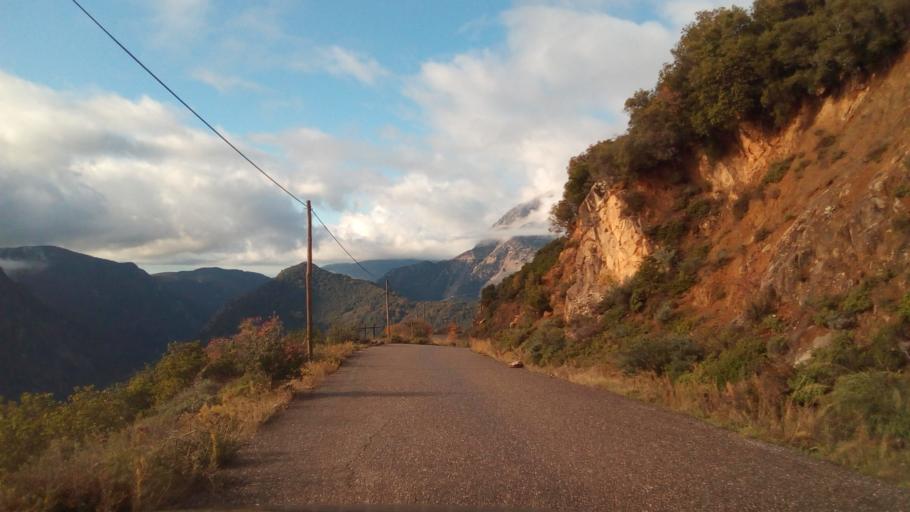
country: GR
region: West Greece
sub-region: Nomos Aitolias kai Akarnanias
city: Nafpaktos
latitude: 38.5150
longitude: 21.9628
